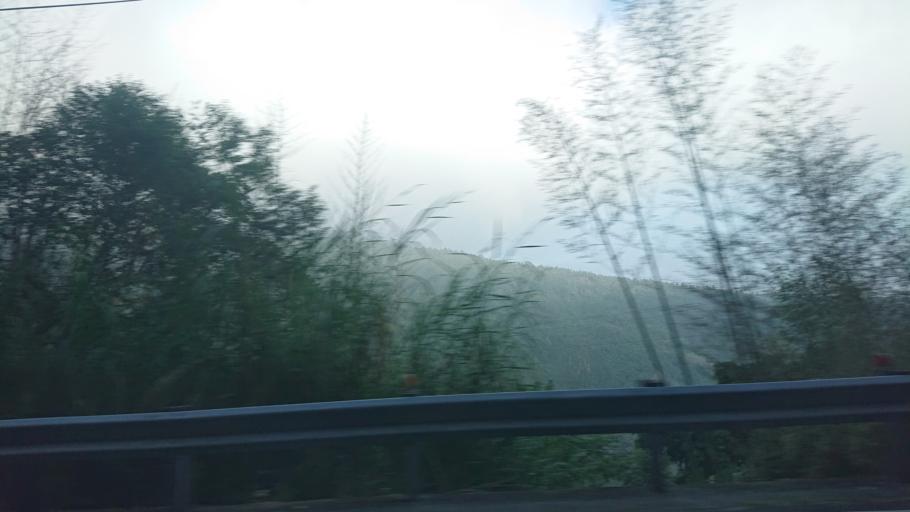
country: TW
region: Taiwan
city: Lugu
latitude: 23.4794
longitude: 120.7364
